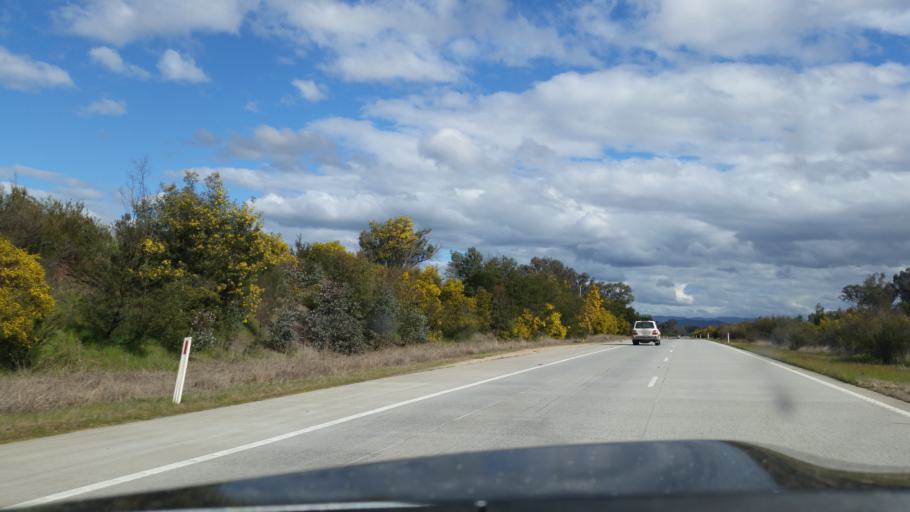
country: AU
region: New South Wales
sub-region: Albury Municipality
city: Lavington
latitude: -36.0102
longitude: 146.9885
